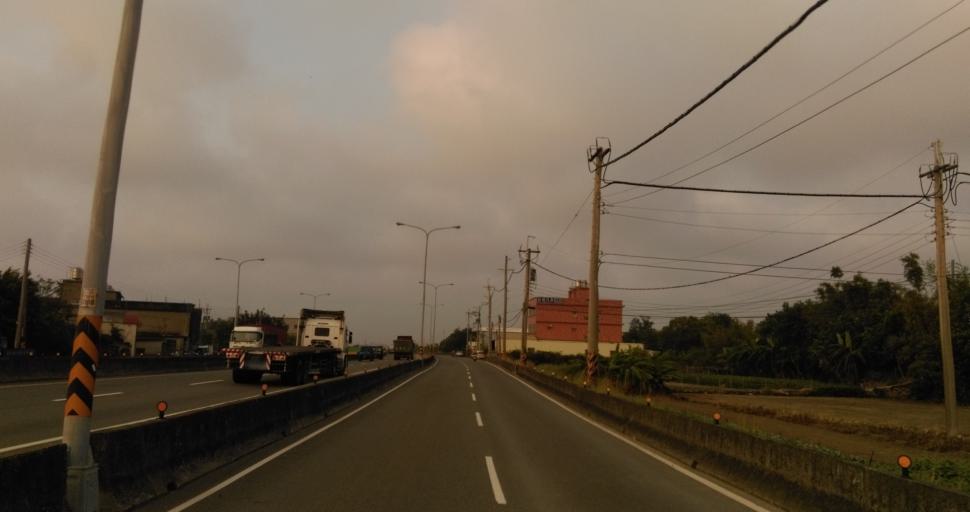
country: TW
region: Taiwan
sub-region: Hsinchu
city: Hsinchu
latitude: 24.7859
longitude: 120.9168
